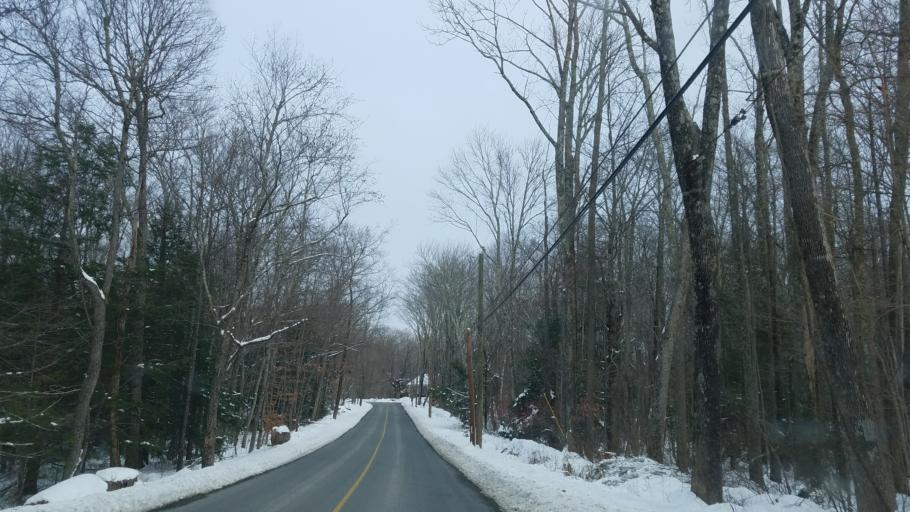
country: US
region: Connecticut
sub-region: Litchfield County
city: New Hartford Center
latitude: 41.8838
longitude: -73.0128
